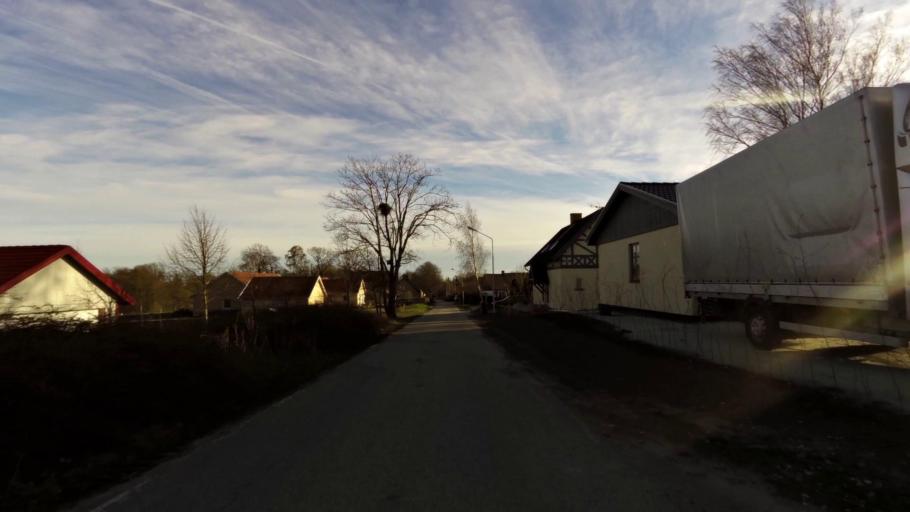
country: SE
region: Skane
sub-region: Kavlinge Kommun
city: Loddekopinge
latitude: 55.7707
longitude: 13.0551
